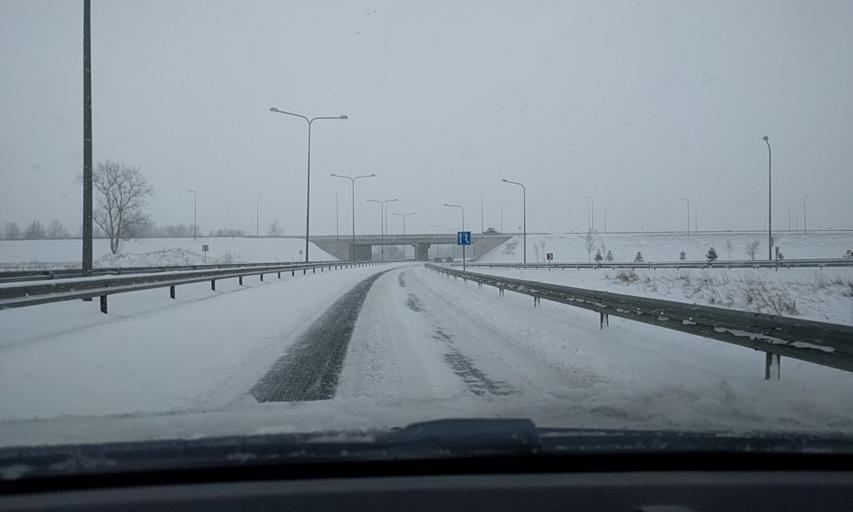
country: EE
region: Harju
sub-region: Joelaehtme vald
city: Loo
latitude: 59.4578
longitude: 24.9832
